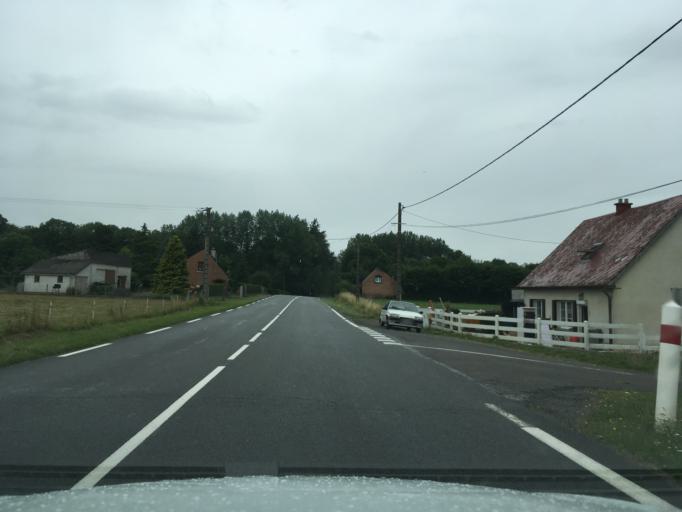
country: FR
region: Picardie
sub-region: Departement de l'Aisne
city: Buironfosse
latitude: 49.9541
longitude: 3.7946
